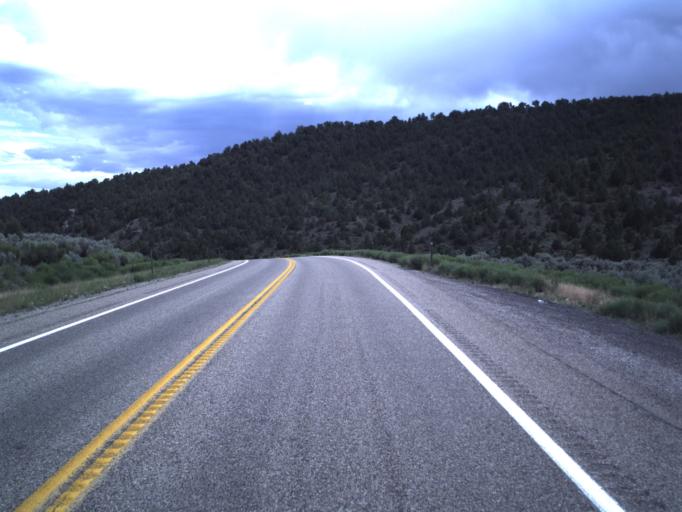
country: US
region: Utah
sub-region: Garfield County
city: Panguitch
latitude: 37.9916
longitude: -112.5018
